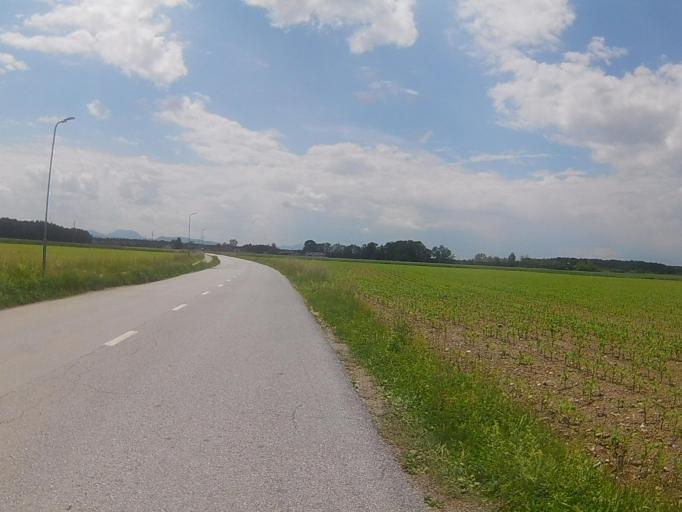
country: SI
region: Kidricevo
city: Kidricevo
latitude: 46.4351
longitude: 15.8121
